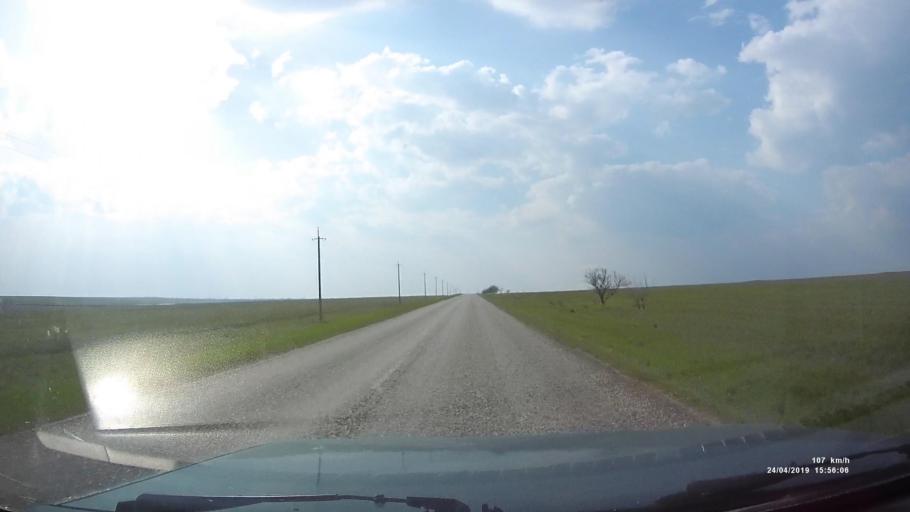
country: RU
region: Kalmykiya
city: Yashalta
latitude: 46.5948
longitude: 42.5372
